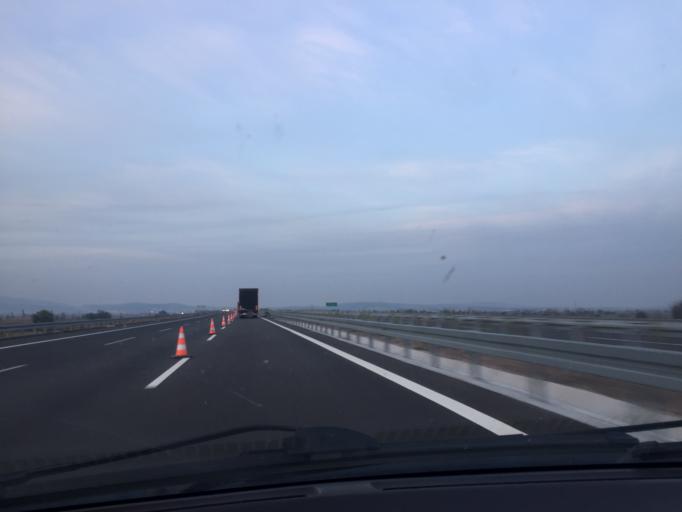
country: TR
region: Manisa
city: Halitpasa
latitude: 38.7277
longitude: 27.6544
